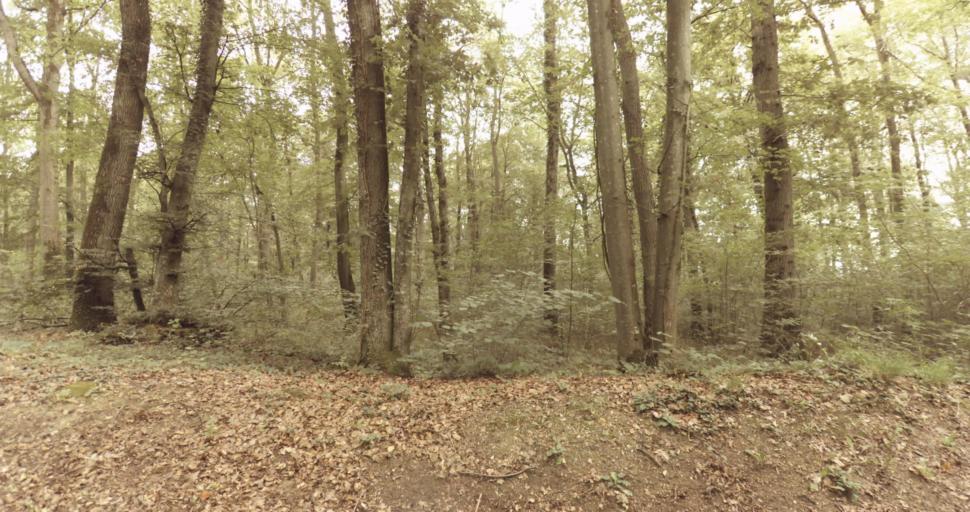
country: FR
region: Haute-Normandie
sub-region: Departement de l'Eure
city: Menilles
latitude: 49.0329
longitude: 1.3128
